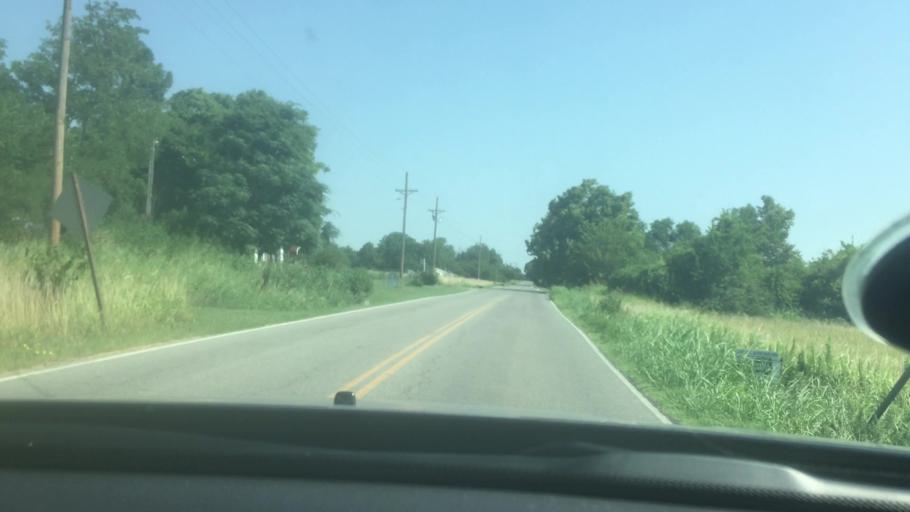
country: US
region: Oklahoma
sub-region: Bryan County
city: Calera
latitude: 34.0351
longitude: -96.4745
